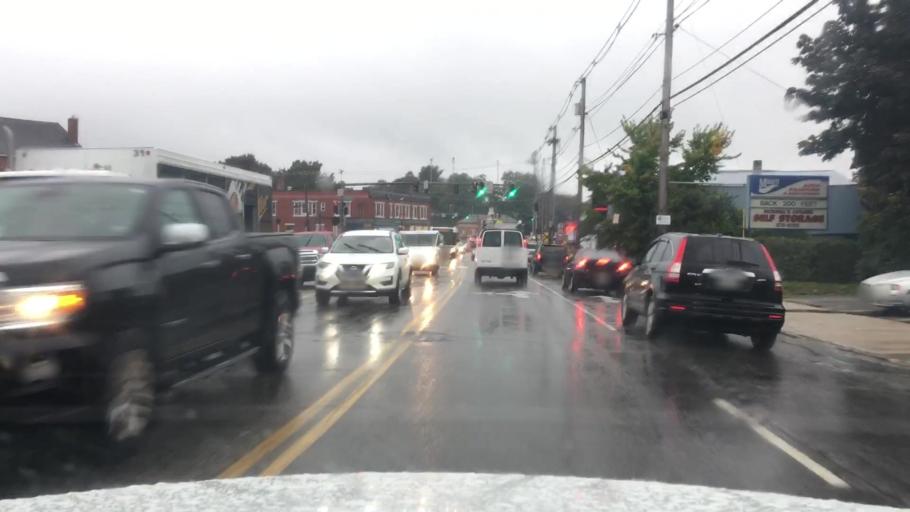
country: US
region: Maine
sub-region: Cumberland County
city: Portland
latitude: 43.6868
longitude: -70.2927
